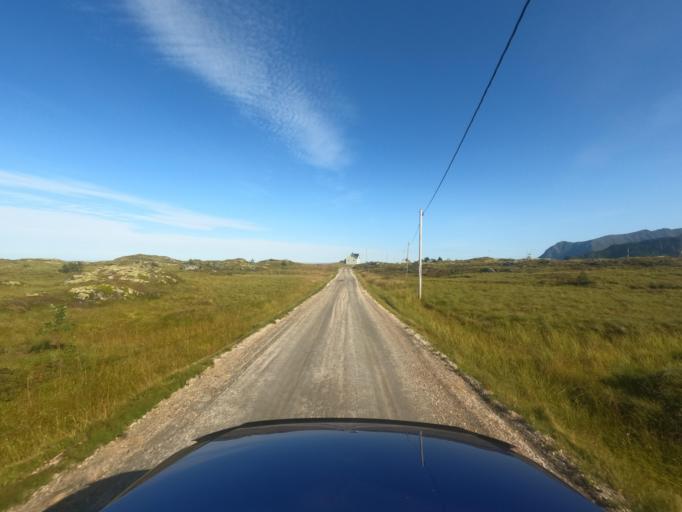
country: NO
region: Nordland
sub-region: Vestvagoy
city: Evjen
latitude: 68.2866
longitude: 13.7859
